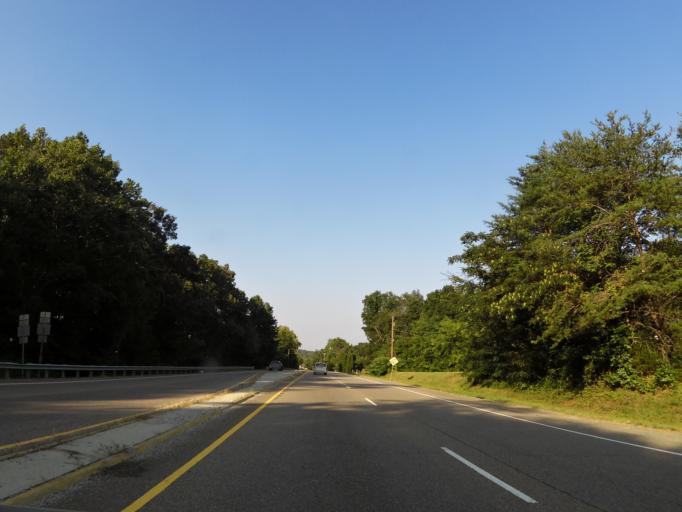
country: US
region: Tennessee
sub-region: Knox County
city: Knoxville
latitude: 35.9095
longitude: -83.8371
